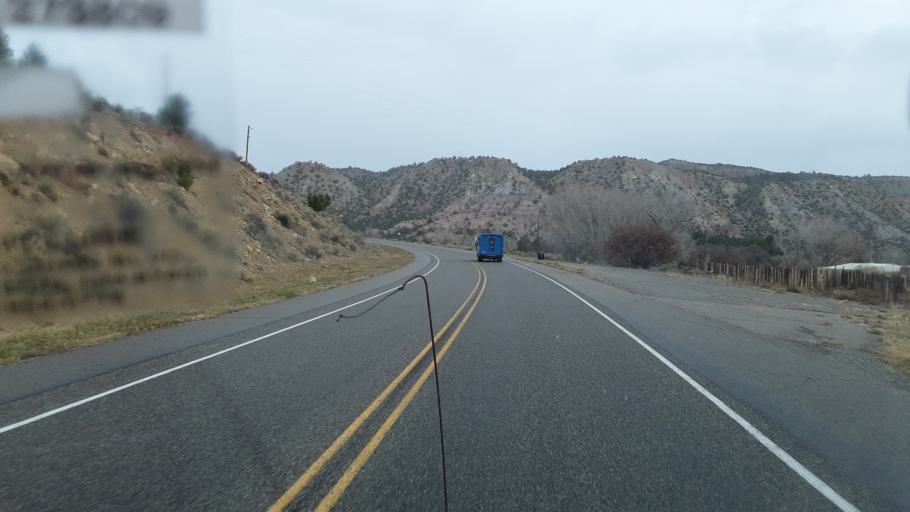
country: US
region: New Mexico
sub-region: Rio Arriba County
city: Santa Teresa
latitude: 36.3887
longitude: -106.4920
